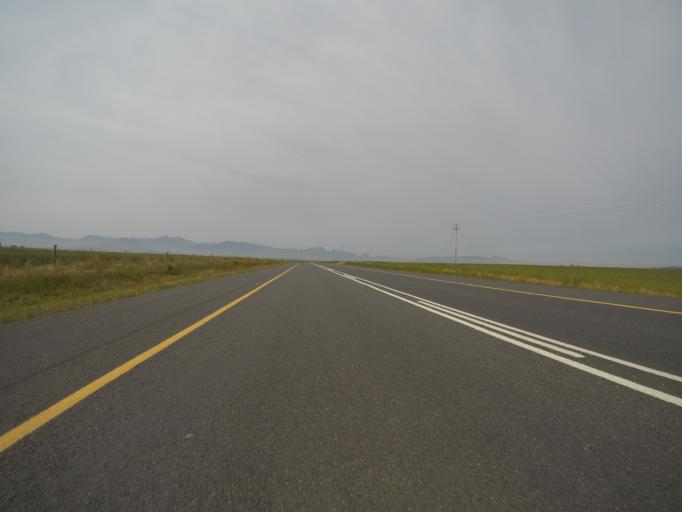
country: ZA
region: Western Cape
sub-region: Cape Winelands District Municipality
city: Noorder-Paarl
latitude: -33.5624
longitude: 18.8809
